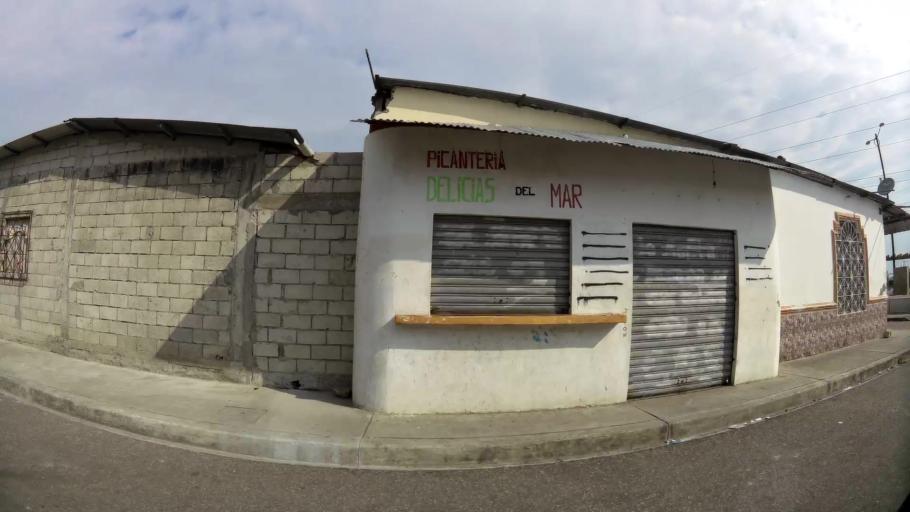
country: EC
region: Guayas
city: Guayaquil
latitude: -2.2491
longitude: -79.9134
